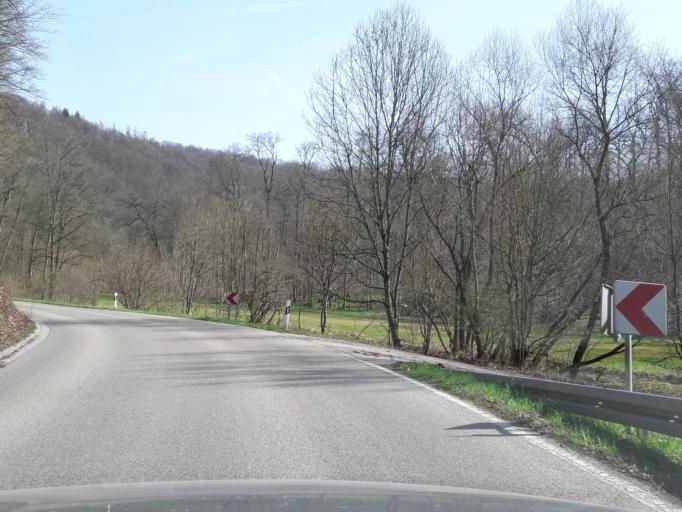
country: DE
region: Baden-Wuerttemberg
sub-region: Regierungsbezirk Stuttgart
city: Ohringen
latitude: 49.2302
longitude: 9.4654
